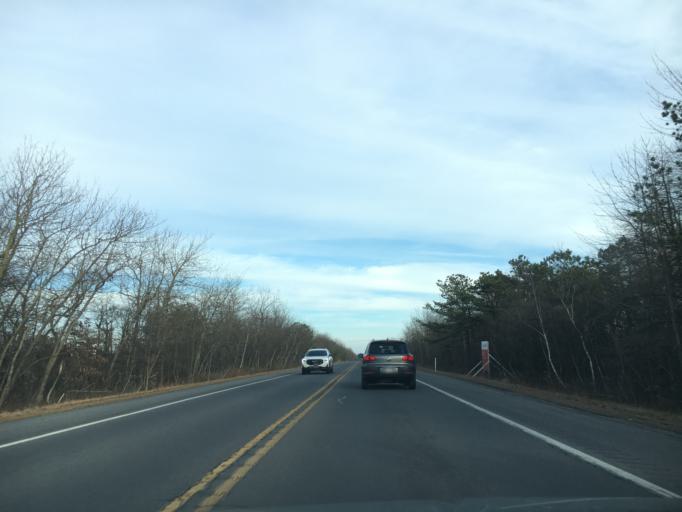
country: US
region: Pennsylvania
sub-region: Luzerne County
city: Hazleton
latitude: 40.9357
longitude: -75.9614
